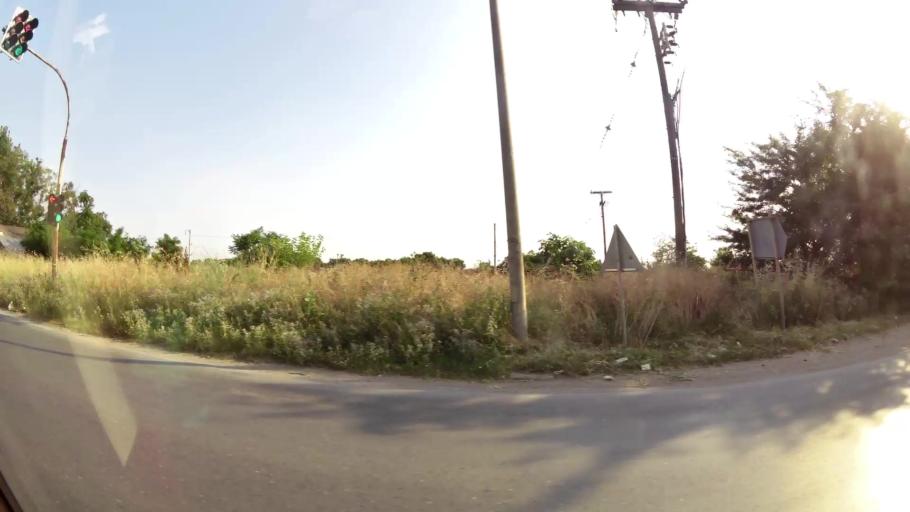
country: GR
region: Central Macedonia
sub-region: Nomos Thessalonikis
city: Diavata
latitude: 40.6792
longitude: 22.8682
